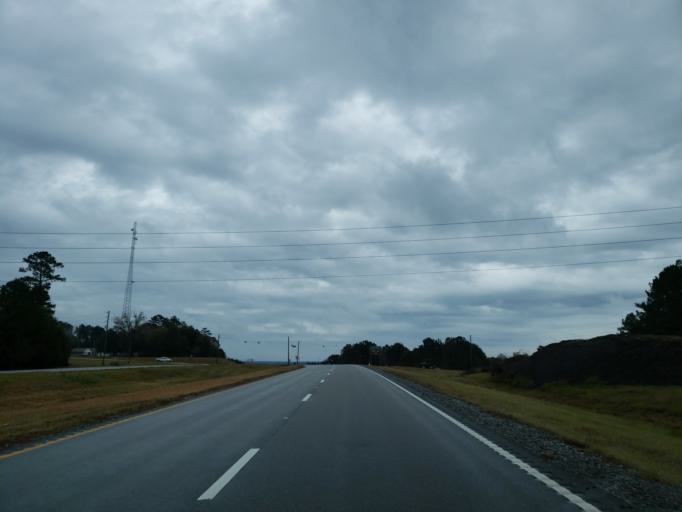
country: US
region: Mississippi
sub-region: Wayne County
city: Waynesboro
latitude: 31.6835
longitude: -88.6953
